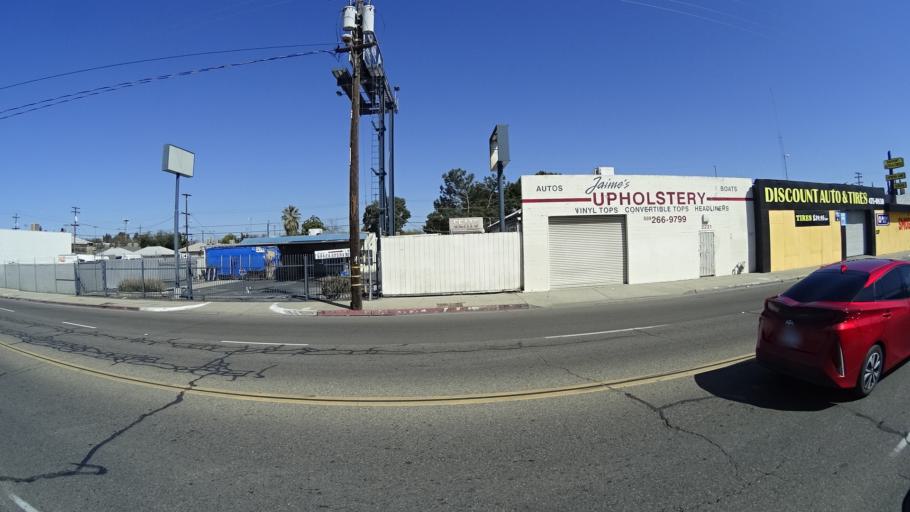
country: US
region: California
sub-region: Fresno County
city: Fresno
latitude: 36.7650
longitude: -119.7850
